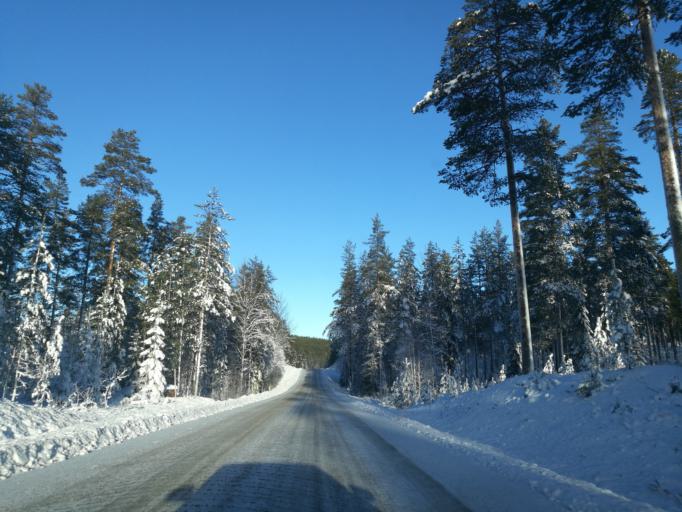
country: NO
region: Hedmark
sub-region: Grue
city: Kirkenaer
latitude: 60.5548
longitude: 12.5345
